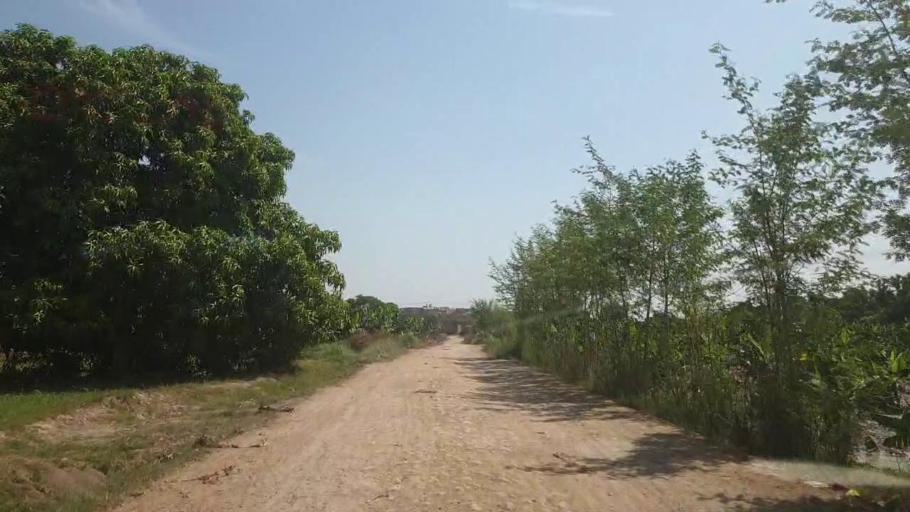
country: PK
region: Sindh
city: Tando Allahyar
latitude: 25.3905
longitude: 68.6723
